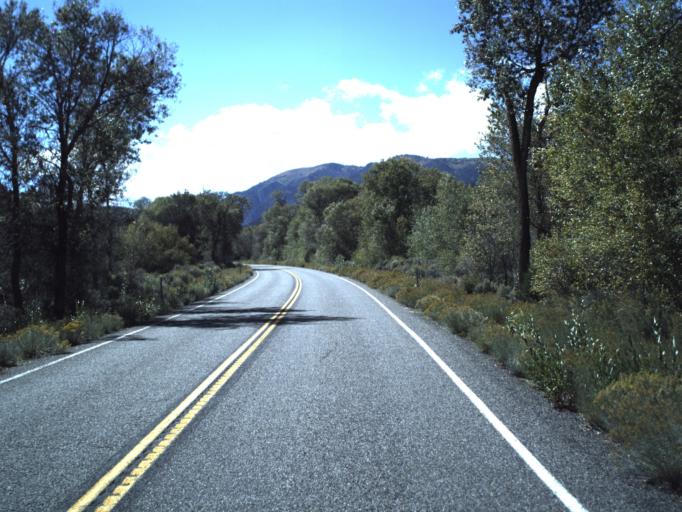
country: US
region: Utah
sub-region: Piute County
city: Junction
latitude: 38.2587
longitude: -112.2765
